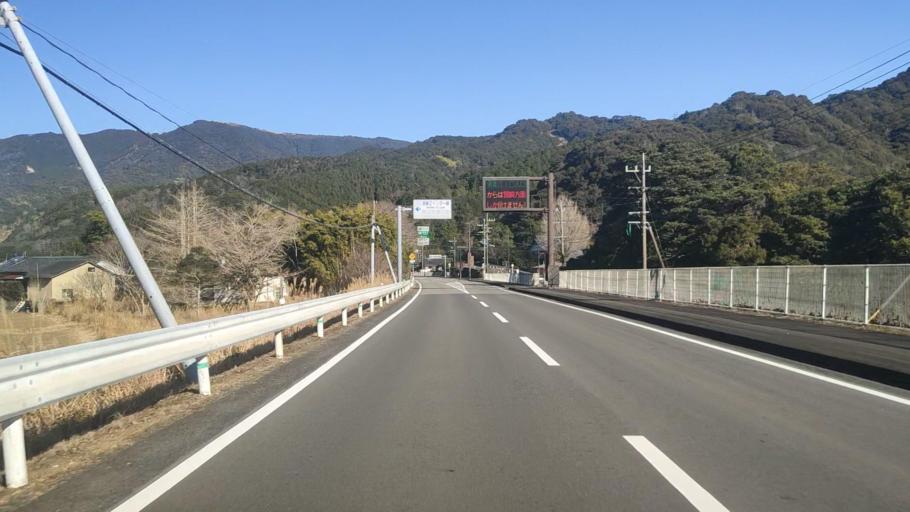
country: JP
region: Miyazaki
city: Nobeoka
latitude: 32.6641
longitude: 131.7666
